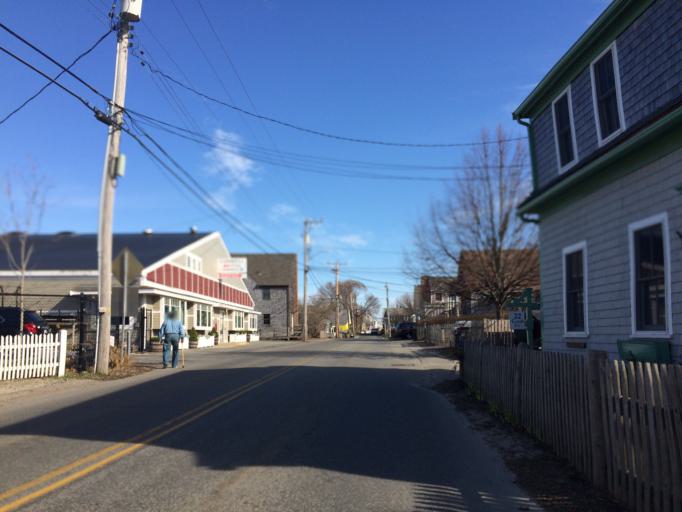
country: US
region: Massachusetts
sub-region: Barnstable County
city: Provincetown
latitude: 42.0564
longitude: -70.1865
